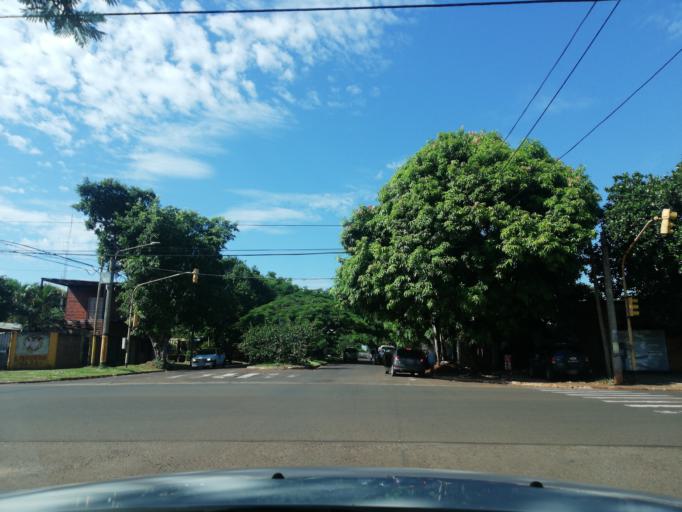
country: AR
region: Misiones
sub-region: Departamento de Capital
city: Posadas
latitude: -27.3780
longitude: -55.9257
